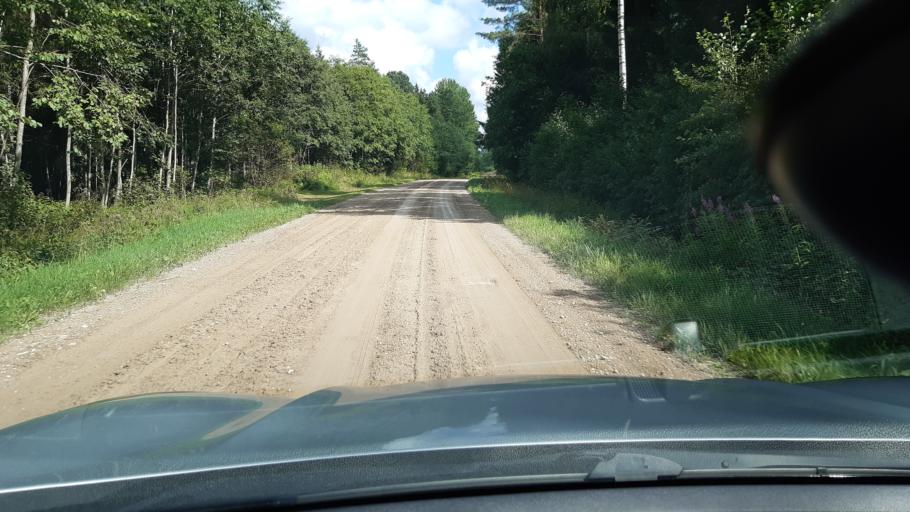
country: EE
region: Jaervamaa
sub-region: Tueri vald
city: Tueri
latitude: 58.9330
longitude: 25.2325
